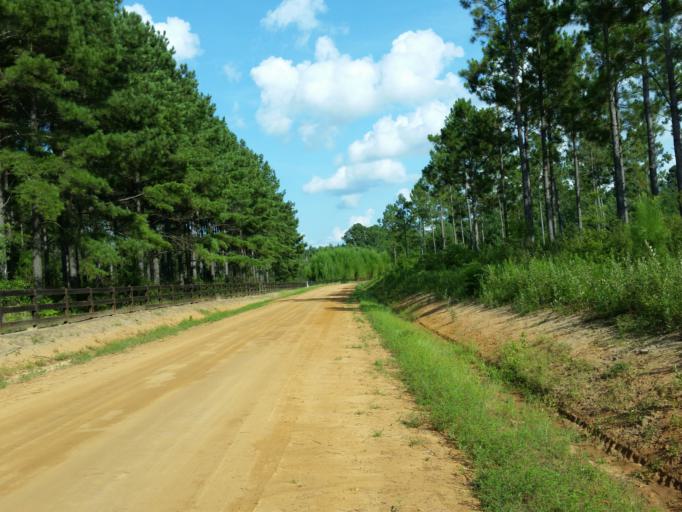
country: US
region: Georgia
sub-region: Lee County
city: Leesburg
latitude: 31.8783
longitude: -84.0393
